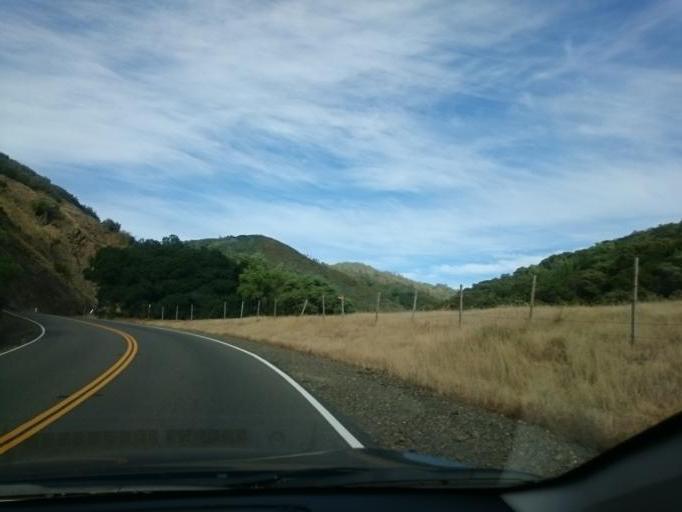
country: US
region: California
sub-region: Napa County
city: Yountville
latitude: 38.4865
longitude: -122.3017
